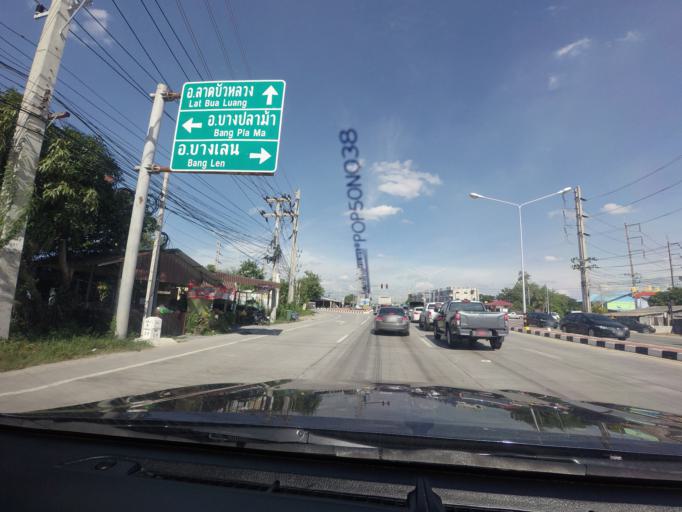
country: TH
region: Suphan Buri
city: Song Phi Nong
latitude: 14.1590
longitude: 100.1070
